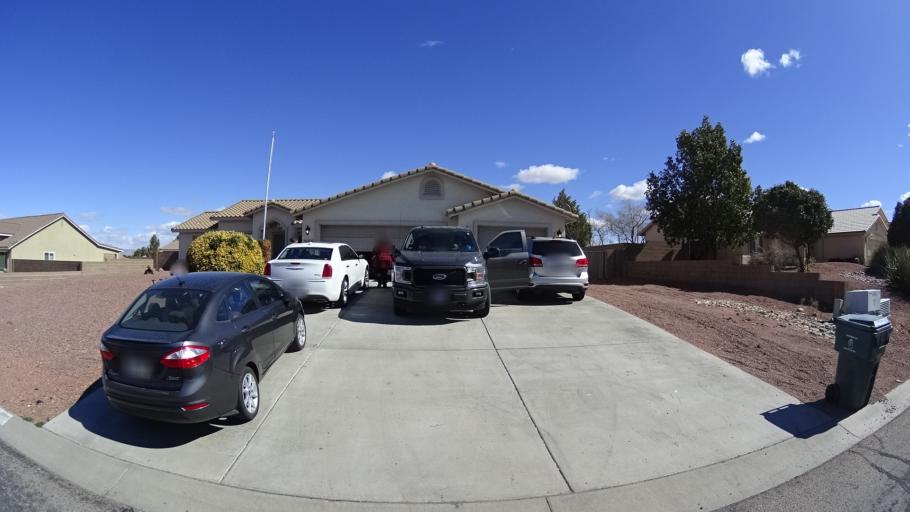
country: US
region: Arizona
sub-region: Mohave County
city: Kingman
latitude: 35.2046
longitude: -113.9744
